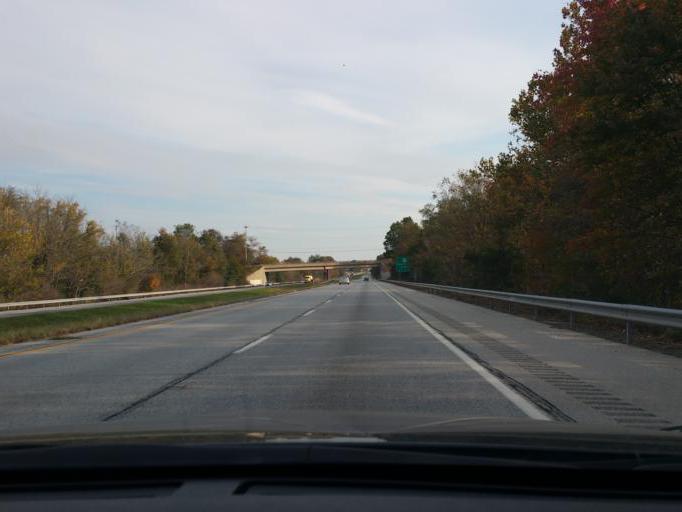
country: US
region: Pennsylvania
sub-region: Chester County
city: Oxford
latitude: 39.7770
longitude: -76.0054
